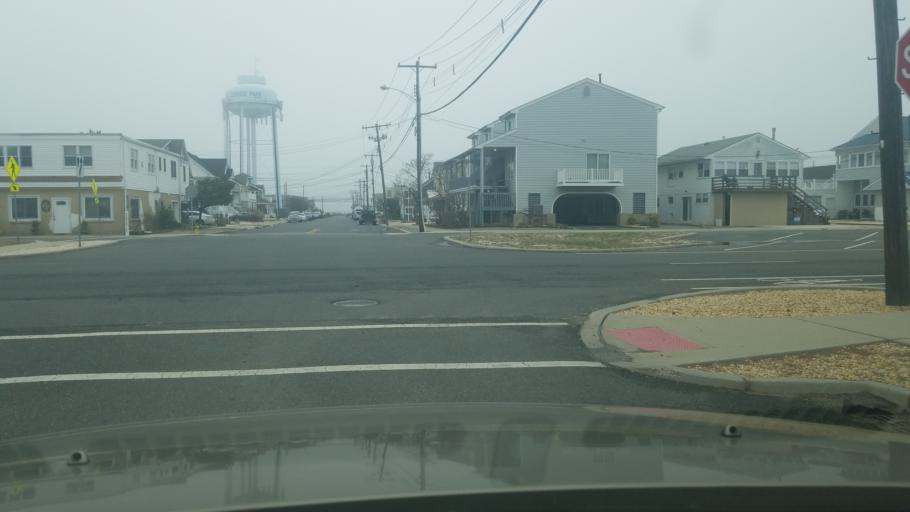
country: US
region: New Jersey
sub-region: Ocean County
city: Seaside Park
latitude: 39.9145
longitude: -74.0796
